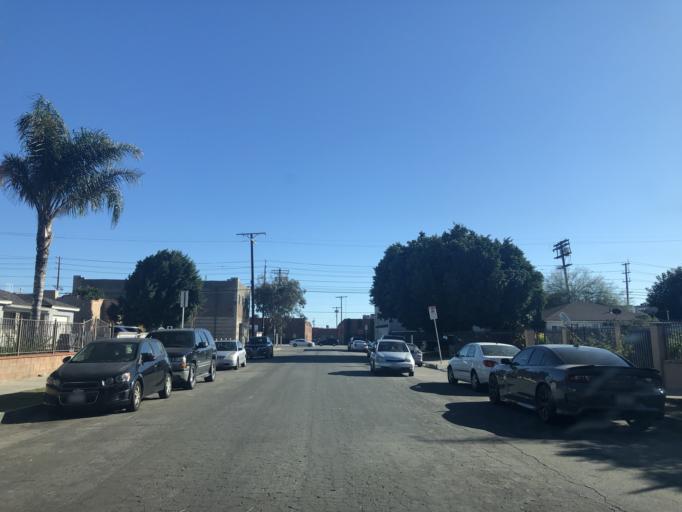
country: US
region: California
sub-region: Los Angeles County
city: North Hollywood
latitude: 34.2251
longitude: -118.3863
